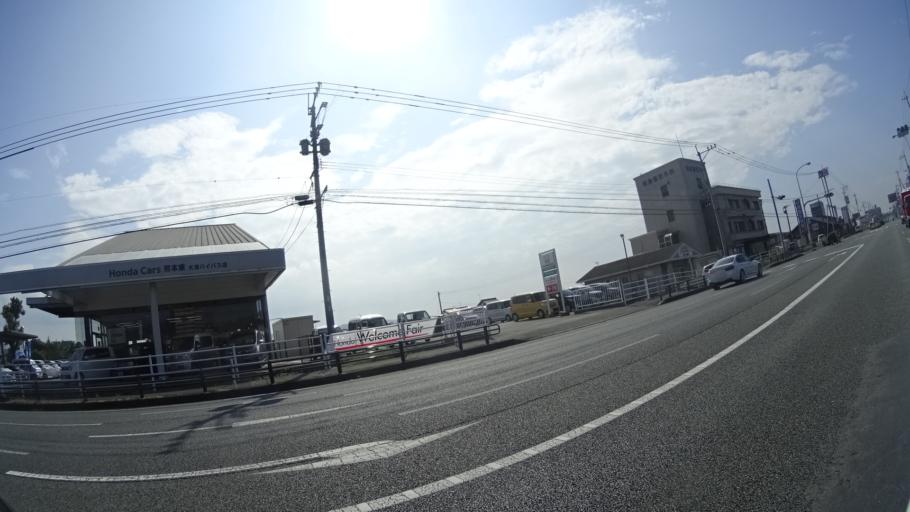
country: JP
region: Kumamoto
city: Ozu
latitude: 32.8756
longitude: 130.8639
